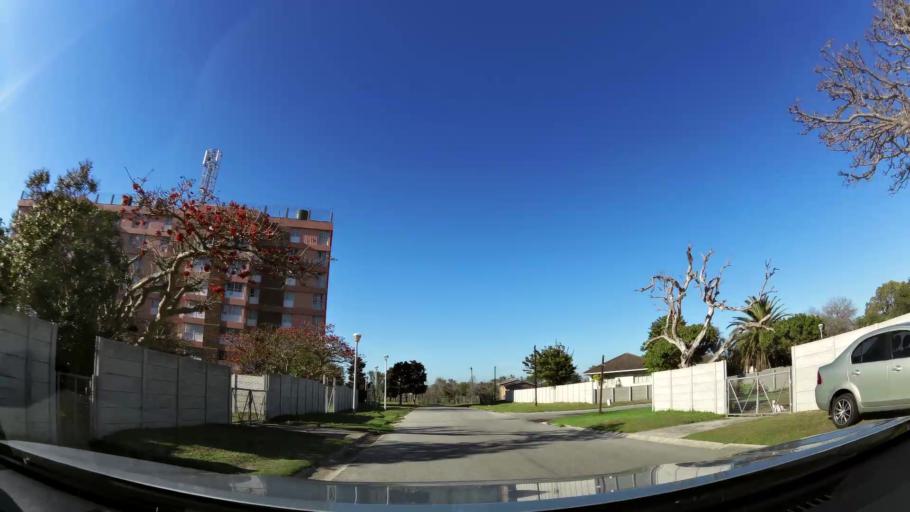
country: ZA
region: Eastern Cape
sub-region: Nelson Mandela Bay Metropolitan Municipality
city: Port Elizabeth
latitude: -33.9890
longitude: 25.6286
